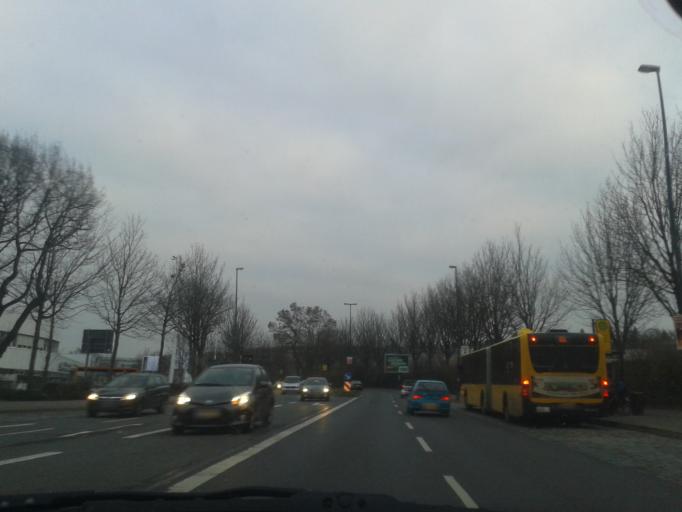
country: DE
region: Saxony
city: Dresden
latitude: 51.0156
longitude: 13.7717
